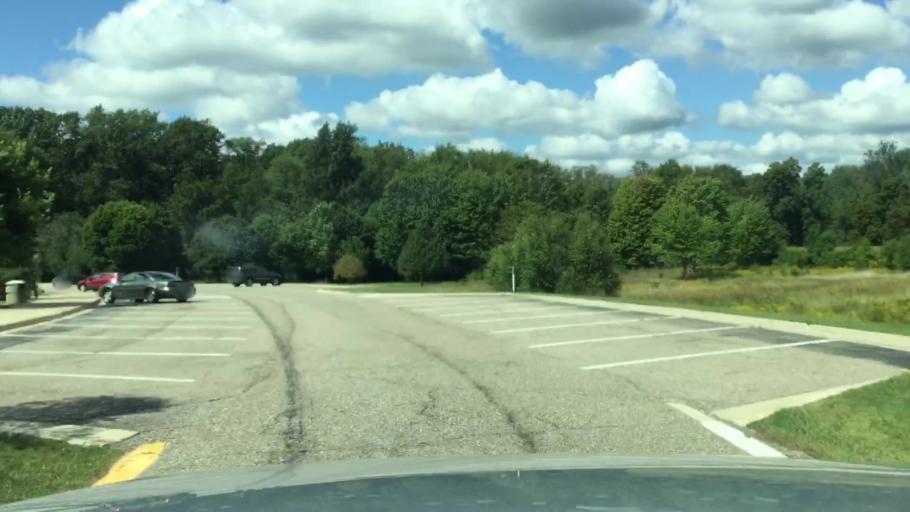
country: US
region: Michigan
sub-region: Calhoun County
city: Marshall
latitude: 42.2837
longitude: -84.9128
